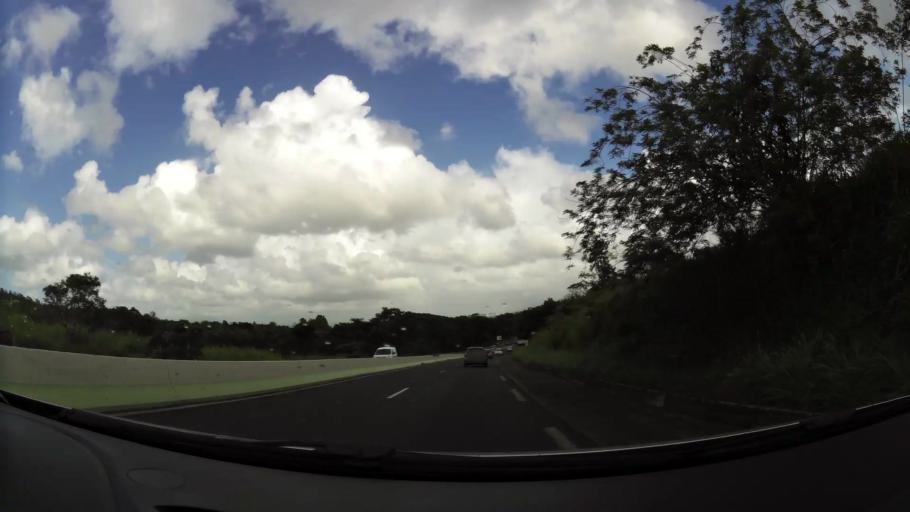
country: MQ
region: Martinique
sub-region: Martinique
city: Les Trois-Ilets
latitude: 14.5188
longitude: -60.9840
